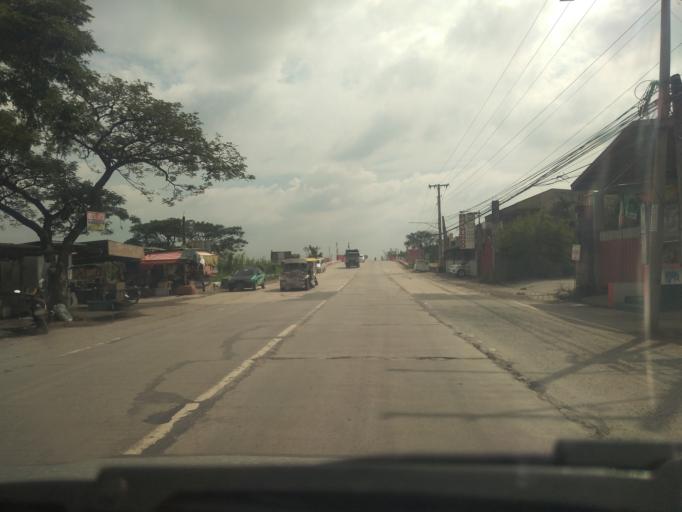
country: PH
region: Central Luzon
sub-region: Province of Pampanga
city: Santo Domingo
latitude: 15.0002
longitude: 120.7285
